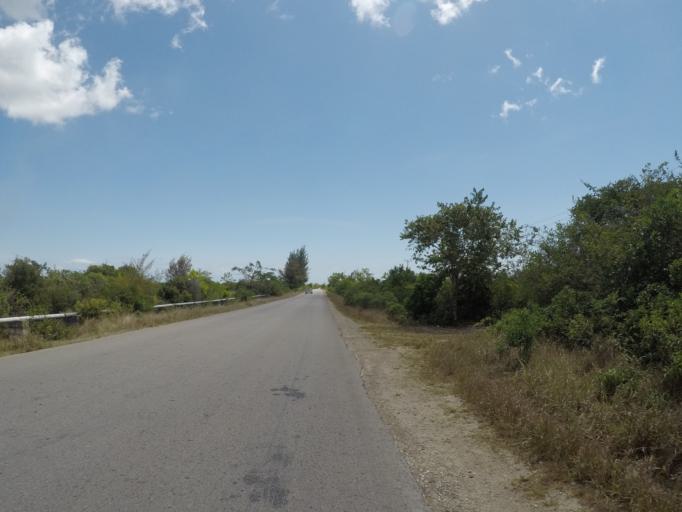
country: TZ
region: Zanzibar Central/South
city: Nganane
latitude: -6.2838
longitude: 39.4630
